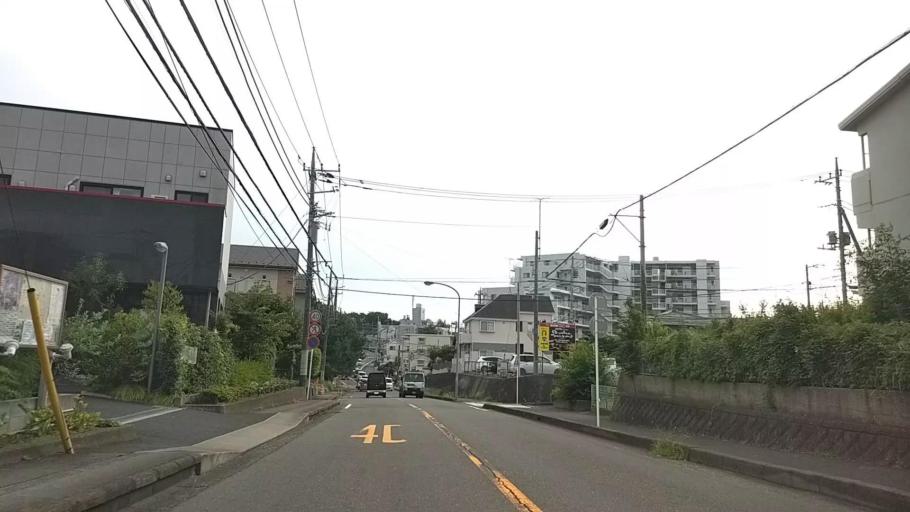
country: JP
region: Kanagawa
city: Minami-rinkan
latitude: 35.4708
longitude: 139.4220
